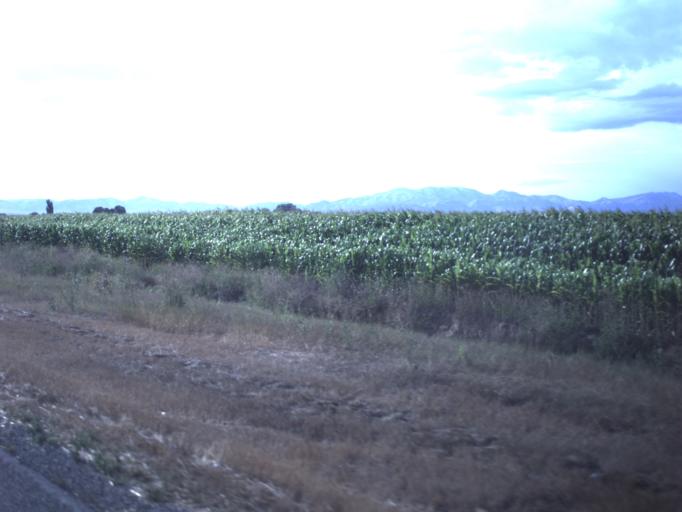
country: US
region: Utah
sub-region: Cache County
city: Lewiston
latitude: 41.9761
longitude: -111.8356
